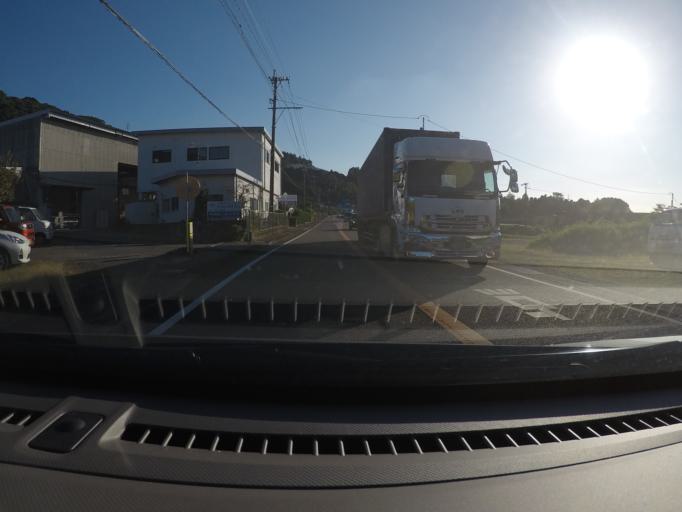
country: JP
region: Kagoshima
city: Izumi
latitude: 32.1526
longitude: 130.3646
